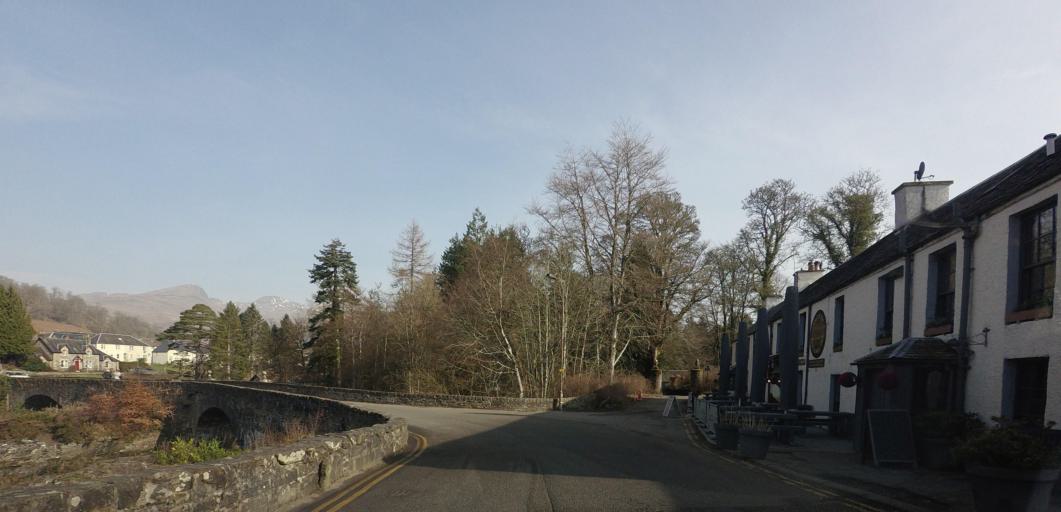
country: GB
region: Scotland
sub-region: Stirling
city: Callander
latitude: 56.4624
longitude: -4.3194
